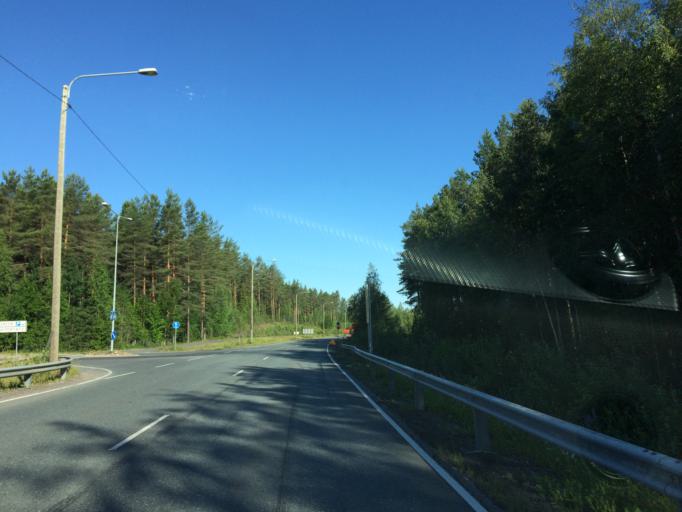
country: FI
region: Haeme
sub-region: Haemeenlinna
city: Haemeenlinna
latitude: 60.9604
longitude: 24.4572
